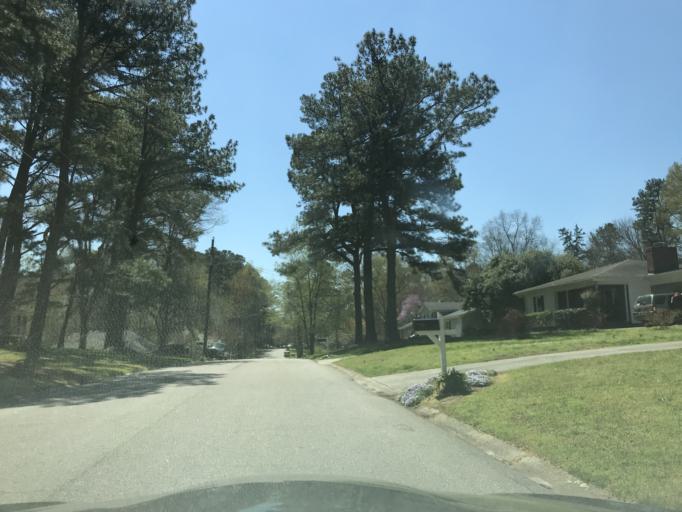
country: US
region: North Carolina
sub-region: Wake County
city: Raleigh
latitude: 35.8213
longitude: -78.5846
